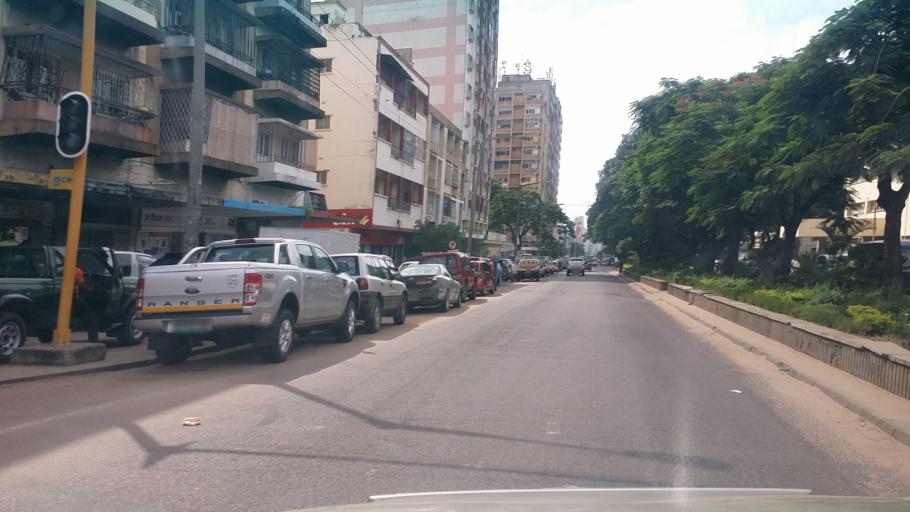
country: MZ
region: Maputo City
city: Maputo
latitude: -25.9584
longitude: 32.5612
